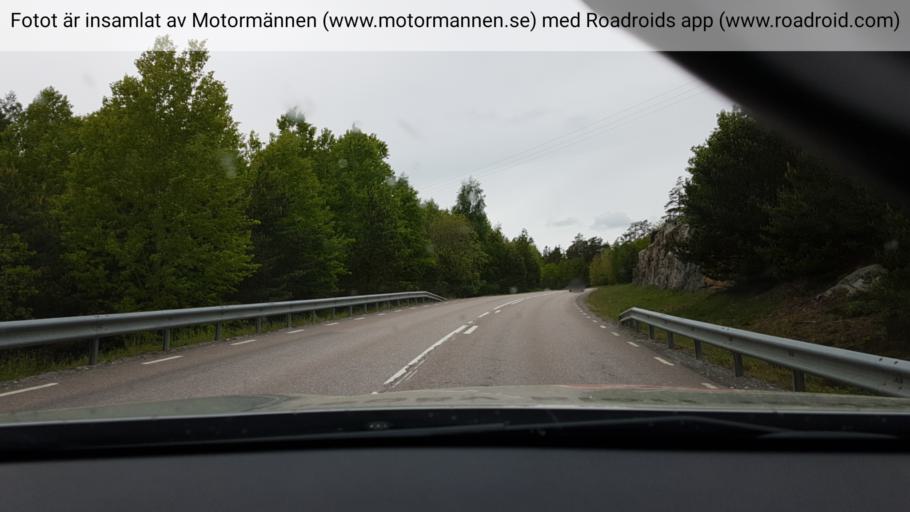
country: SE
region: Stockholm
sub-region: Vaxholms Kommun
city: Vaxholm
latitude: 59.3939
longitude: 18.4074
